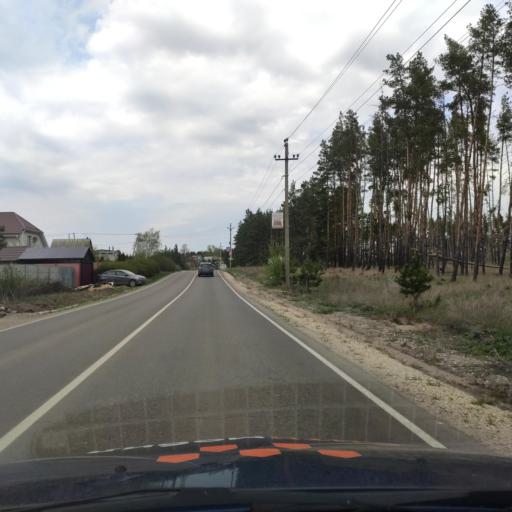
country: RU
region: Voronezj
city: Podgornoye
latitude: 51.8352
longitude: 39.1435
